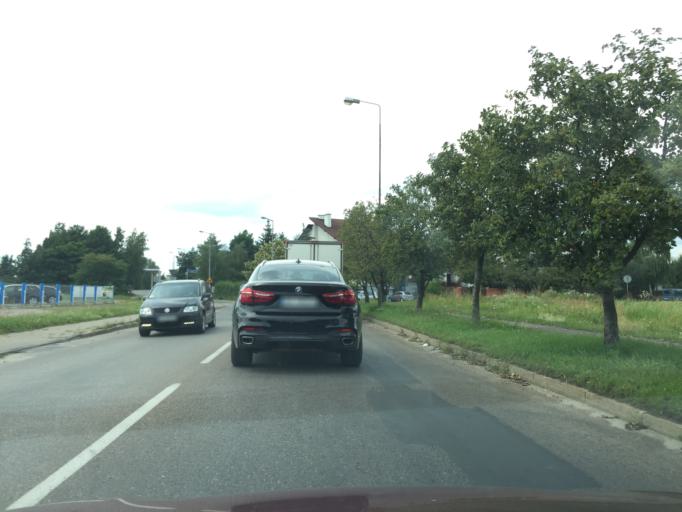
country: PL
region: Greater Poland Voivodeship
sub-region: Kalisz
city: Kalisz
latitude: 51.7396
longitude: 18.0901
